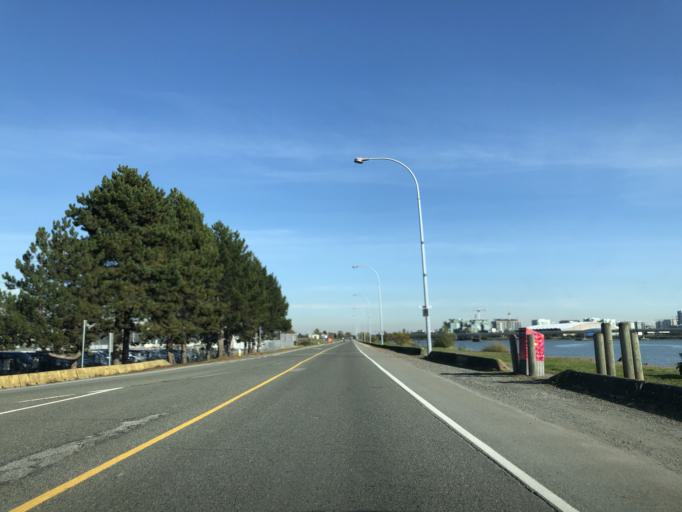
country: CA
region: British Columbia
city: Richmond
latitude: 49.1781
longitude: -123.1653
